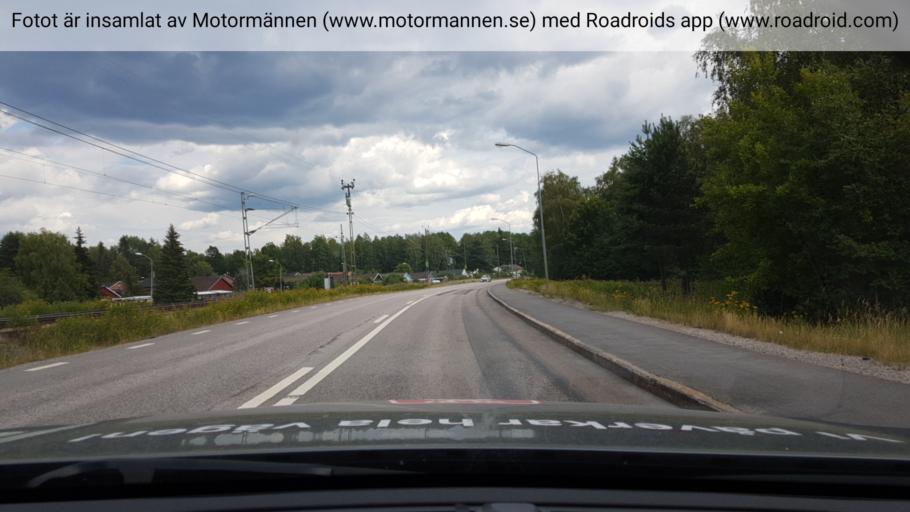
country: SE
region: Uppsala
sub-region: Heby Kommun
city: Morgongava
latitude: 59.9321
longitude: 16.9663
